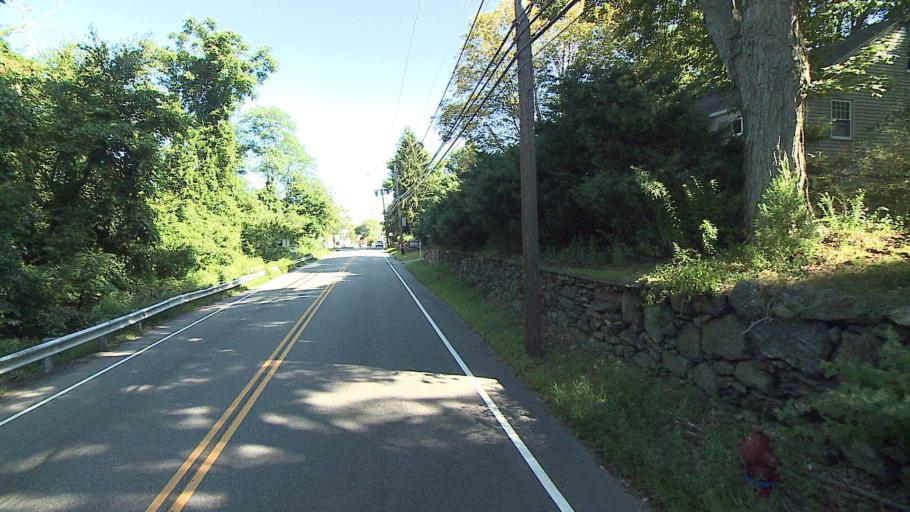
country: US
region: Connecticut
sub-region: New London County
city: Norwich
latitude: 41.5070
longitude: -72.0760
